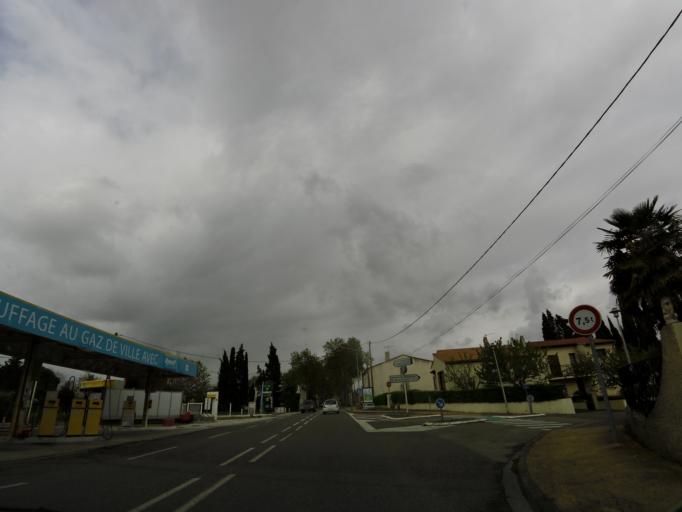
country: FR
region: Languedoc-Roussillon
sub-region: Departement de l'Aude
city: Castelnaudary
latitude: 43.3131
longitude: 1.9659
